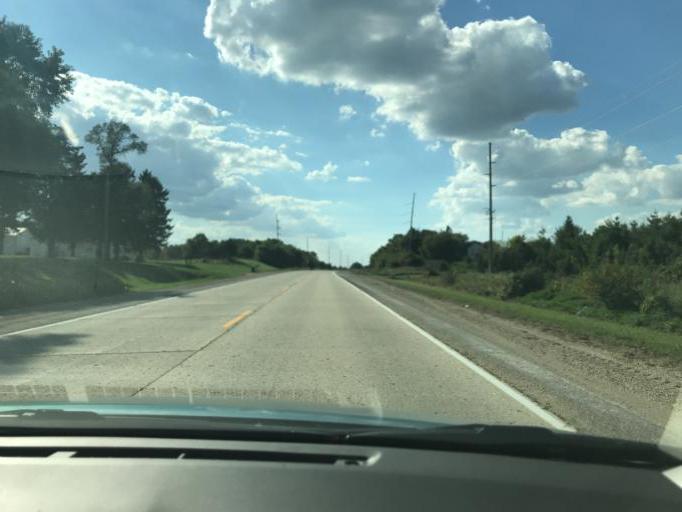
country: US
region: Wisconsin
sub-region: Rock County
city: Orfordville
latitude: 42.5575
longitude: -89.3000
